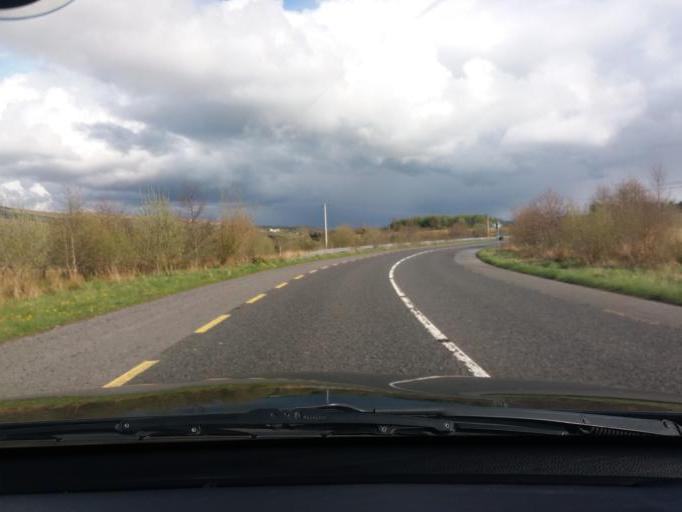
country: IE
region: Connaught
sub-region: County Leitrim
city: Manorhamilton
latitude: 54.3481
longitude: -8.2385
